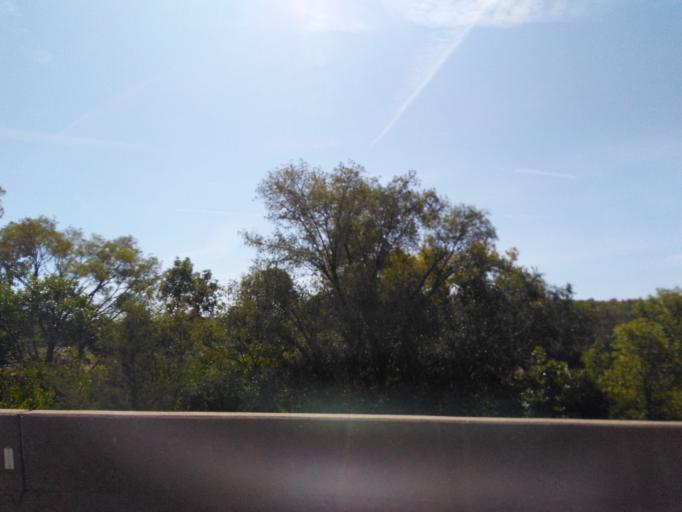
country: US
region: Illinois
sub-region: Saint Clair County
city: Cahokia
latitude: 38.5456
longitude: -90.1699
